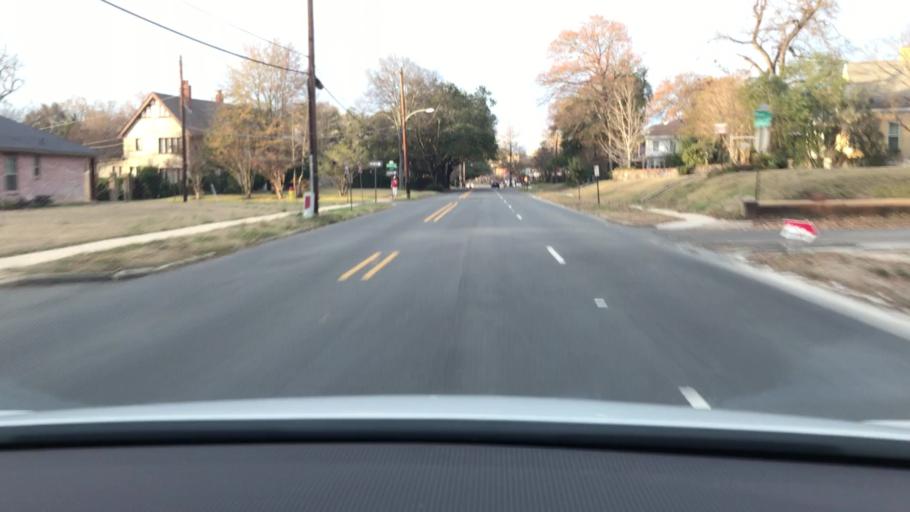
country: US
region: Louisiana
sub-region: Bossier Parish
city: Bossier City
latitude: 32.4887
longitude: -93.7502
